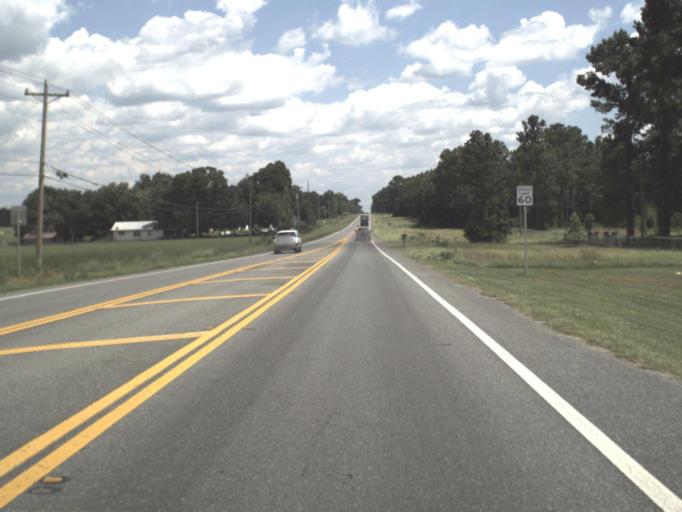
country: US
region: Florida
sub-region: Columbia County
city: Watertown
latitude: 30.1186
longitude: -82.6174
